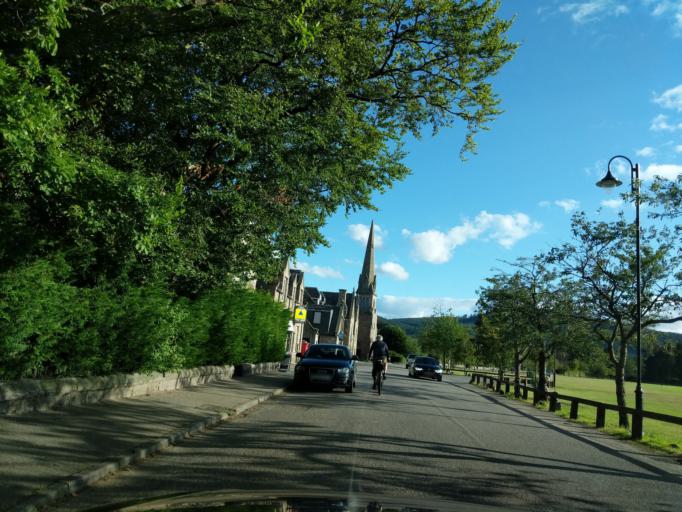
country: GB
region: Scotland
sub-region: Aberdeenshire
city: Aboyne
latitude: 57.0749
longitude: -2.7799
